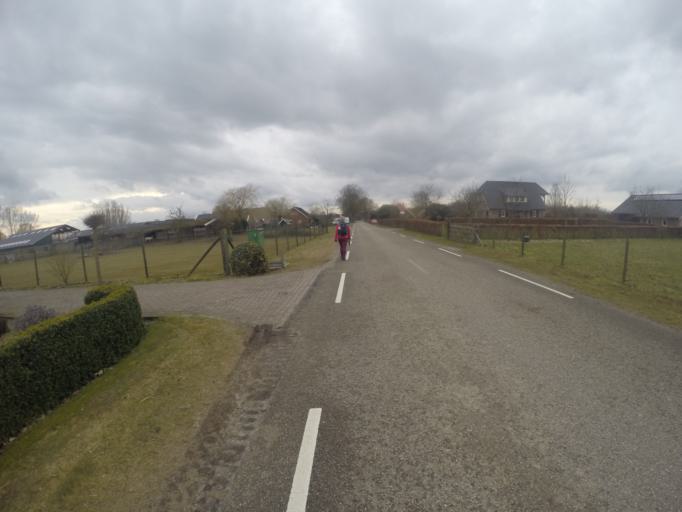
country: NL
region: Gelderland
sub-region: Gemeente Bronckhorst
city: Hengelo
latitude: 52.0485
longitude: 6.3279
